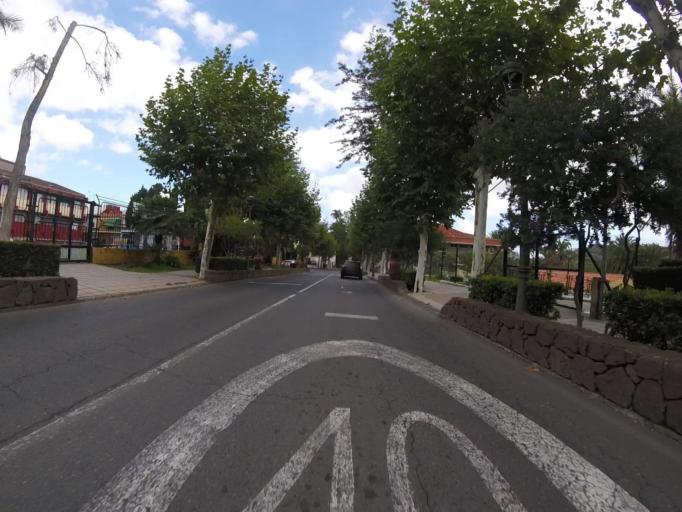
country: ES
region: Canary Islands
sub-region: Provincia de Las Palmas
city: Santa Brigida
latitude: 28.0345
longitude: -15.4970
